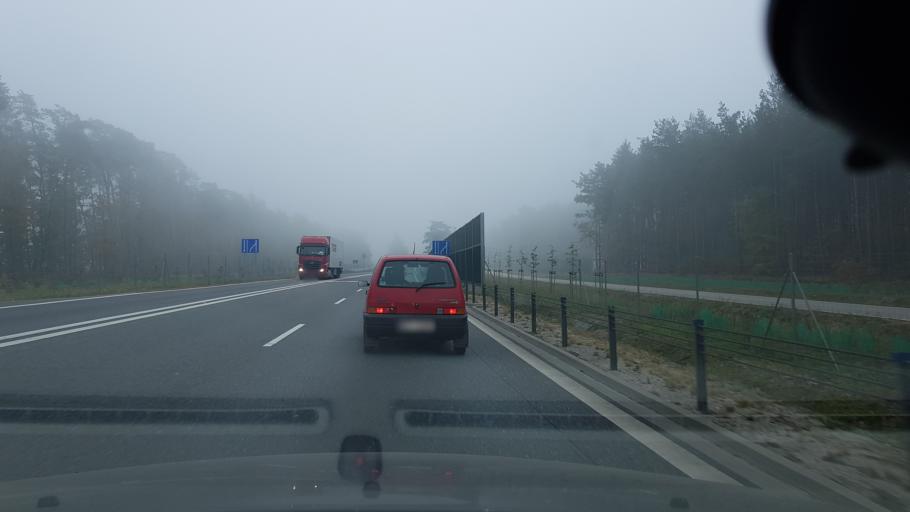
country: PL
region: Masovian Voivodeship
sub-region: Powiat zyrardowski
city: Mszczonow
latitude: 52.0100
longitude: 20.4838
